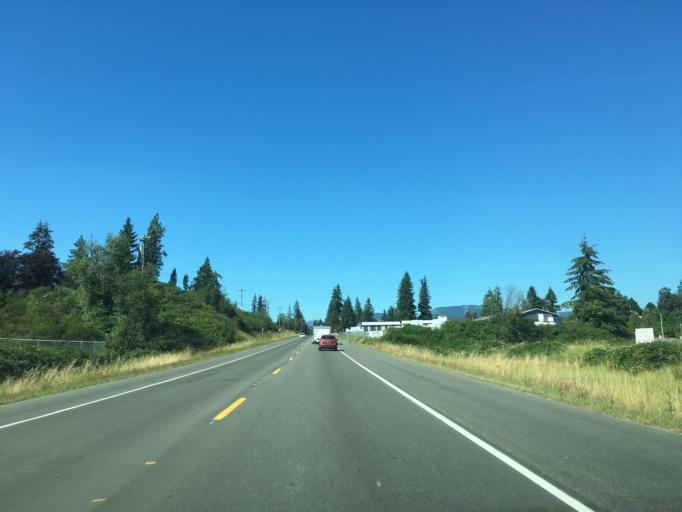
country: US
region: Washington
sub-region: Snohomish County
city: Arlington
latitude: 48.1835
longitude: -122.1287
